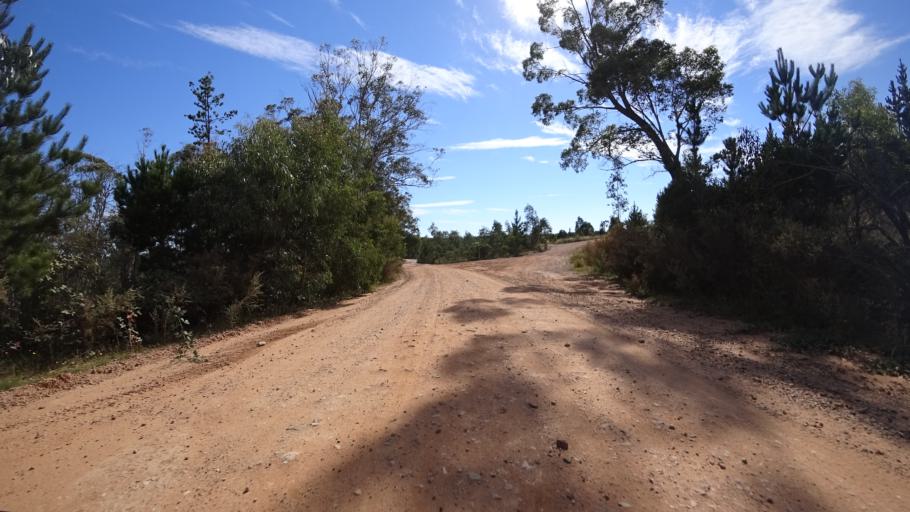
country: AU
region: New South Wales
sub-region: Lithgow
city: Lithgow
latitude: -33.3578
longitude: 150.2519
